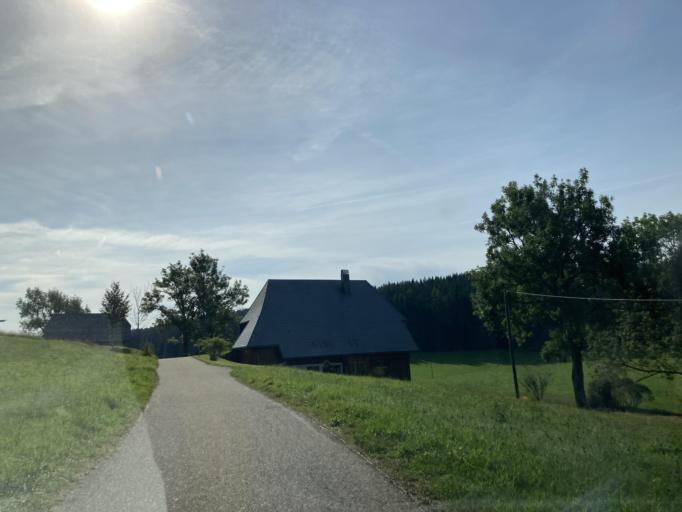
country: DE
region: Baden-Wuerttemberg
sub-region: Freiburg Region
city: Schonwald im Schwarzwald
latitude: 48.0946
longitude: 8.2254
